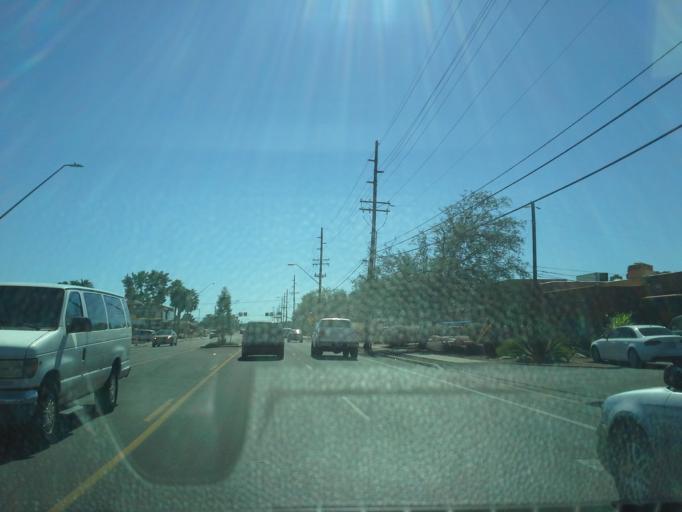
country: US
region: Arizona
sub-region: Pima County
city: Catalina Foothills
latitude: 32.2630
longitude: -110.9439
